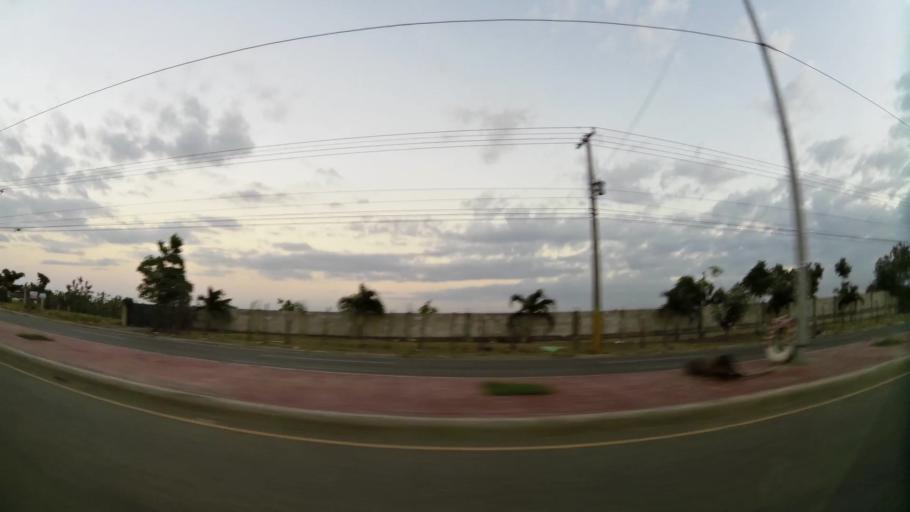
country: DO
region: Nacional
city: La Agustina
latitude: 18.5506
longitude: -69.9476
